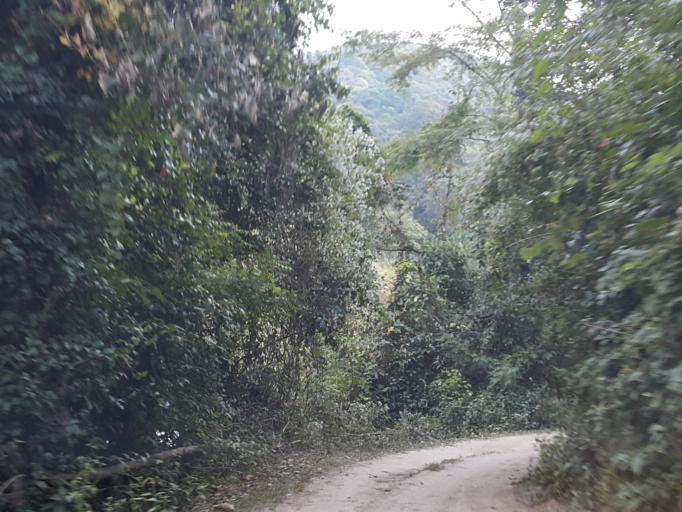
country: TH
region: Chiang Mai
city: Om Koi
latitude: 17.7799
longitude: 98.3010
